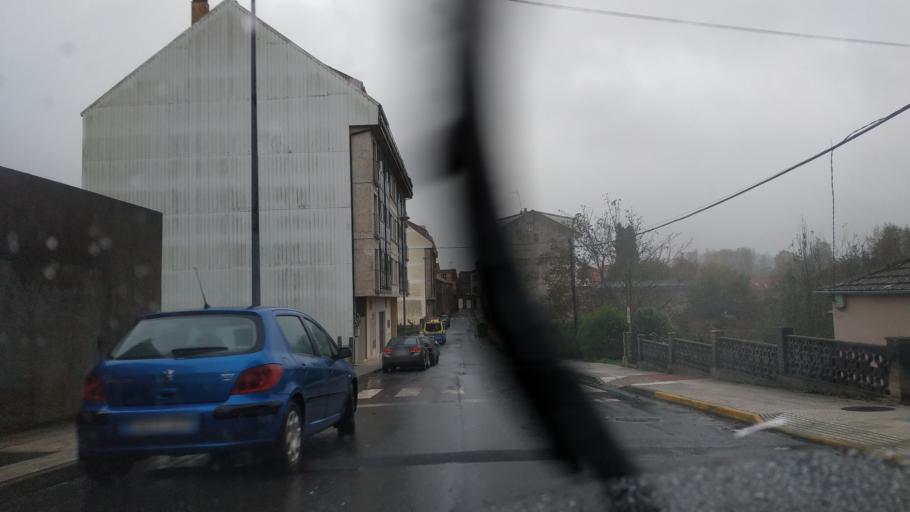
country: ES
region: Galicia
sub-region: Provincia da Coruna
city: Negreira
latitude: 42.9097
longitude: -8.7389
